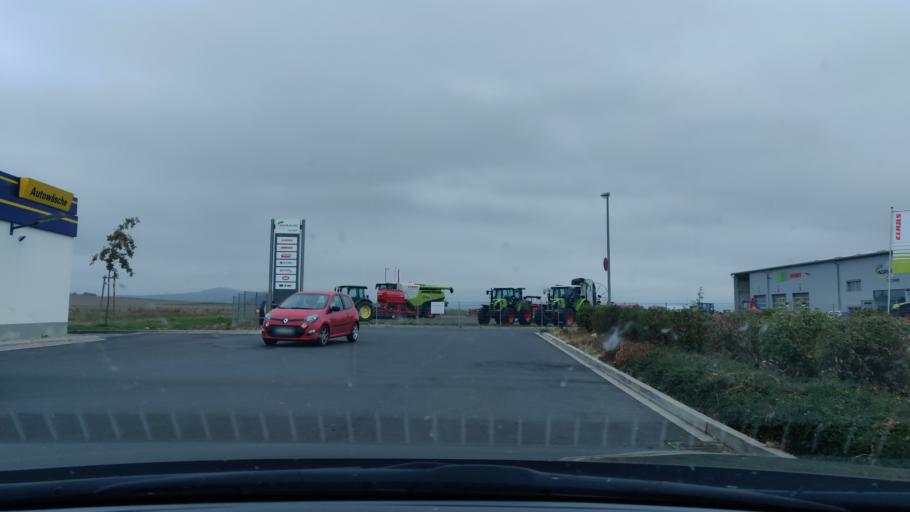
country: DE
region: Hesse
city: Fritzlar
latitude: 51.1403
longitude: 9.2752
